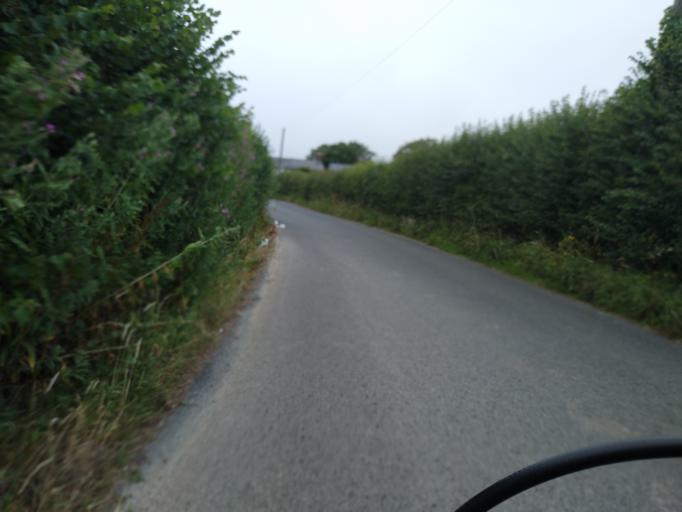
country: GB
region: England
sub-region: Isle of Wight
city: Sandown
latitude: 50.6702
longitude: -1.1624
